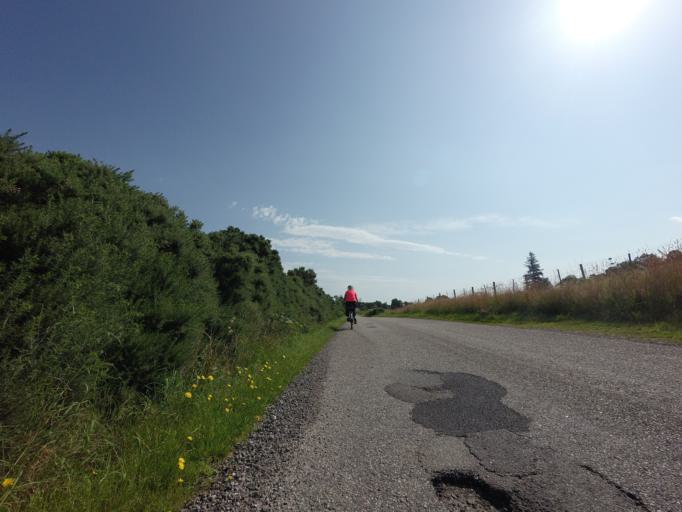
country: GB
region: Scotland
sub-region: Highland
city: Alness
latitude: 57.7078
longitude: -4.2362
